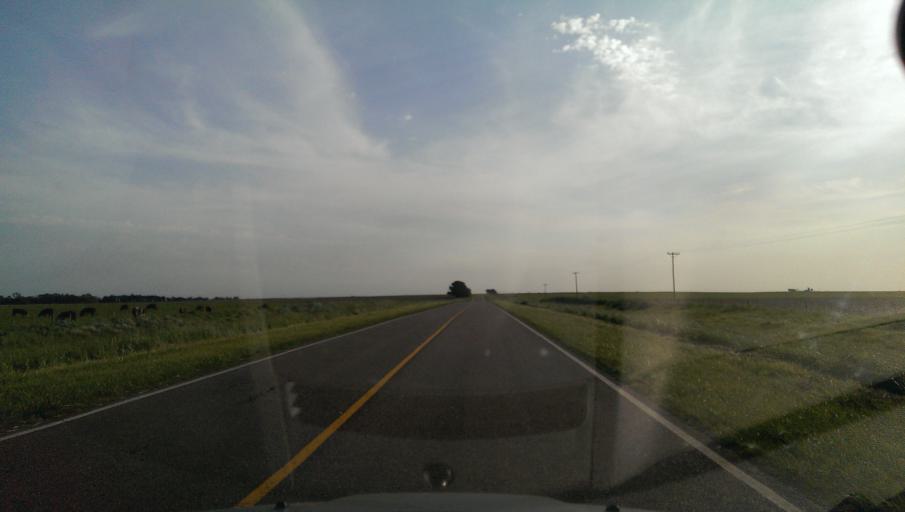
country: AR
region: Buenos Aires
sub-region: Partido de General La Madrid
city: General La Madrid
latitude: -37.5880
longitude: -61.3702
